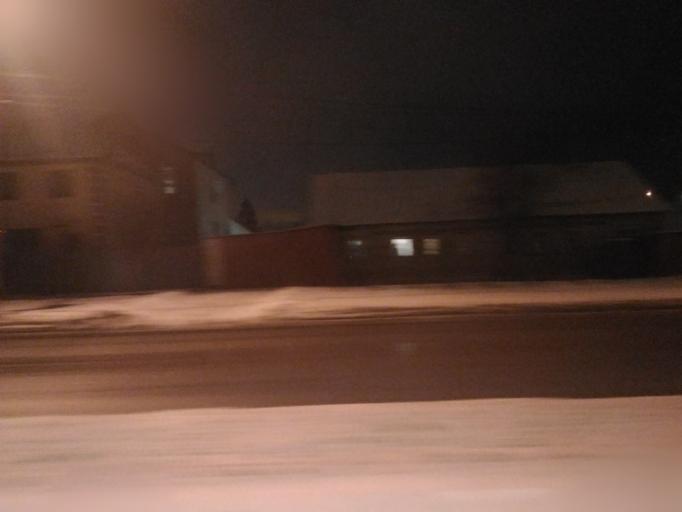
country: RU
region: Ulyanovsk
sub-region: Ulyanovskiy Rayon
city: Ulyanovsk
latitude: 54.3574
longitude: 48.3753
